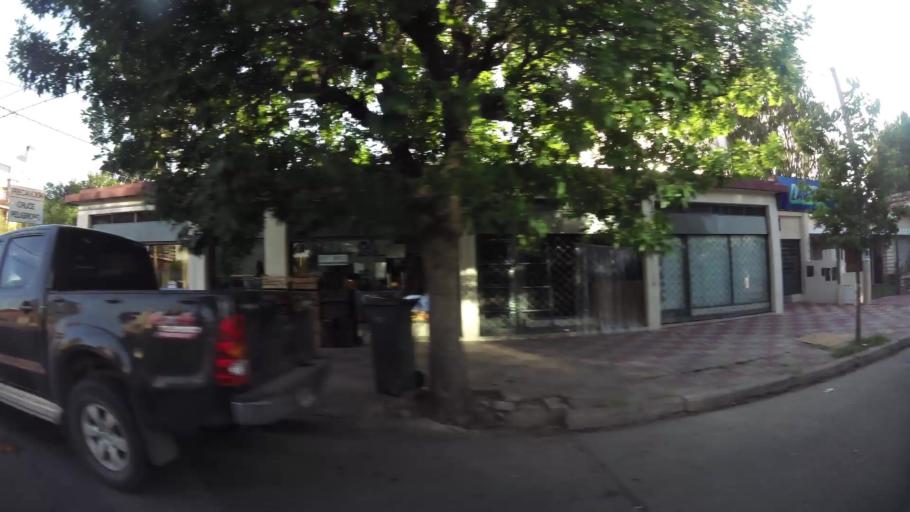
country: AR
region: Cordoba
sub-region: Departamento de Capital
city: Cordoba
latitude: -31.3792
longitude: -64.2274
